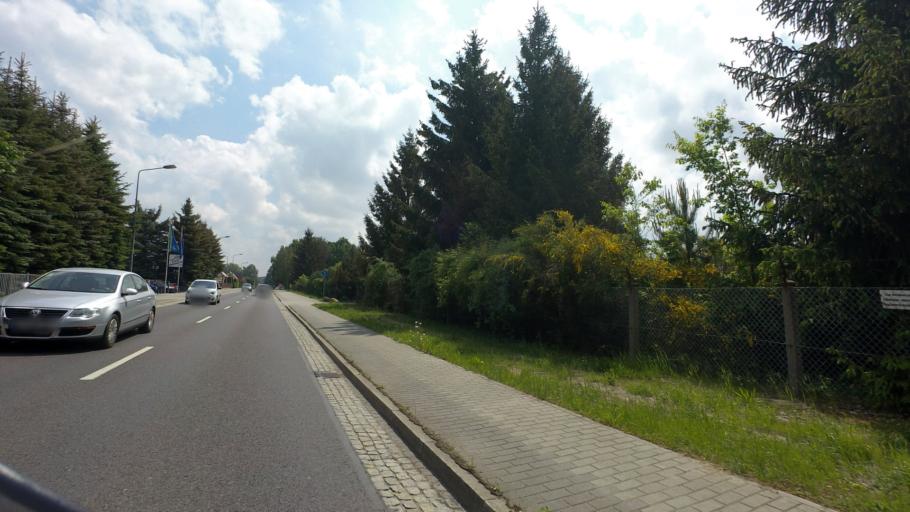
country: DE
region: Saxony
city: Weisswasser
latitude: 51.5166
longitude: 14.6087
